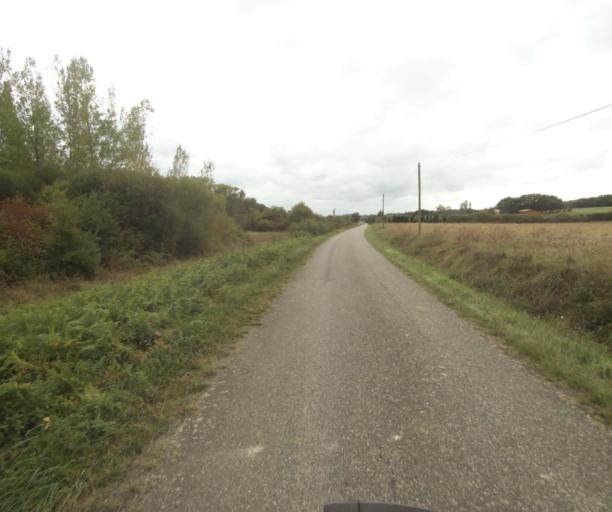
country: FR
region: Midi-Pyrenees
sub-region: Departement de la Haute-Garonne
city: Launac
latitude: 43.8371
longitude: 1.1053
